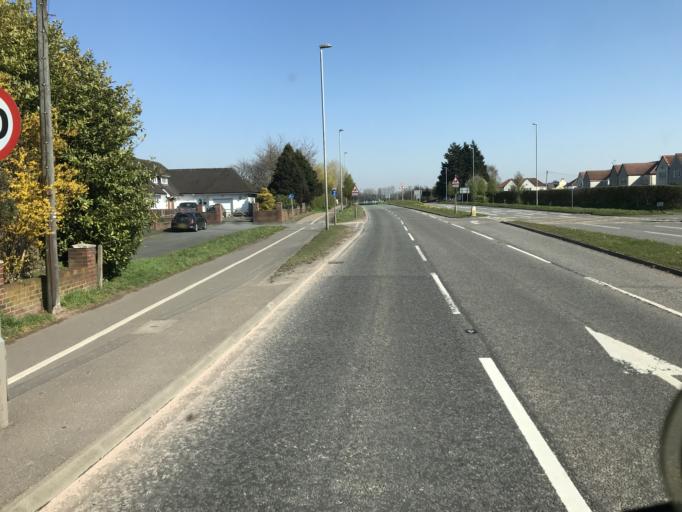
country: GB
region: England
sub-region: Cheshire West and Chester
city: Hoole
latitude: 53.1882
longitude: -2.8536
